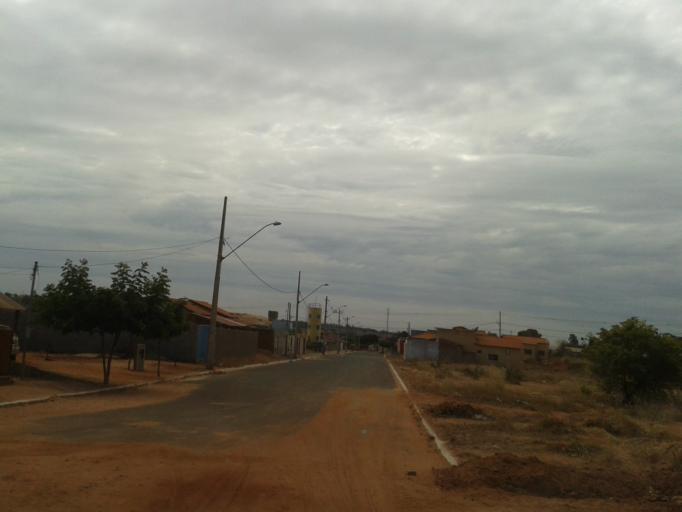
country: BR
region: Minas Gerais
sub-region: Santa Vitoria
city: Santa Vitoria
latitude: -18.8506
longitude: -50.1354
